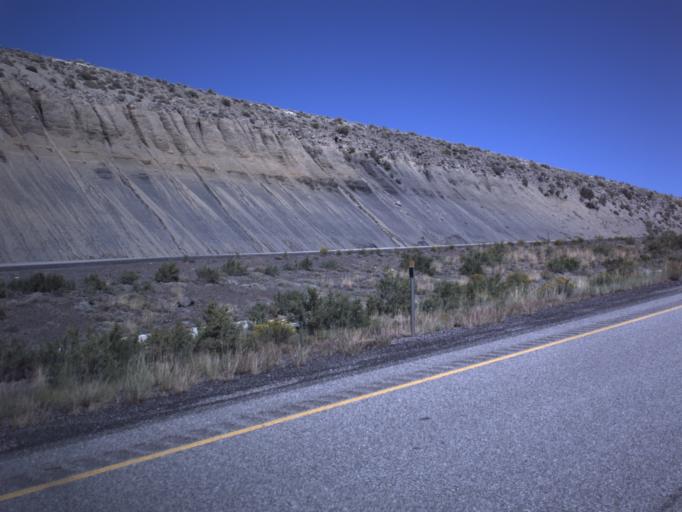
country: US
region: Utah
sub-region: Emery County
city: Ferron
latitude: 38.7682
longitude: -111.3412
